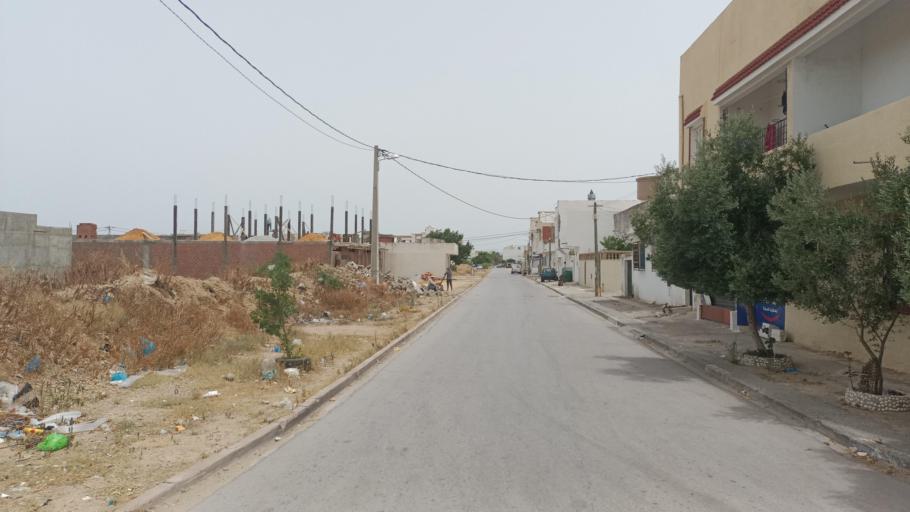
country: TN
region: Nabul
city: Manzil Bu Zalafah
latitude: 36.6990
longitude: 10.4840
